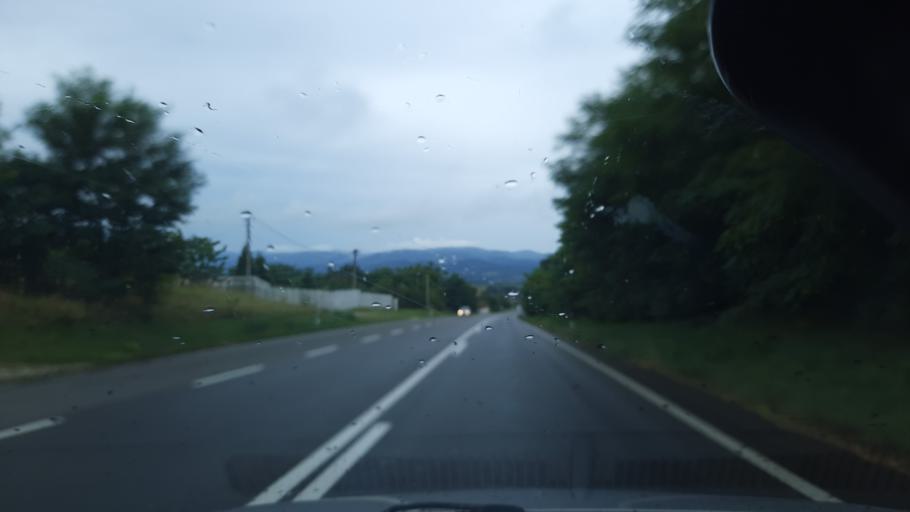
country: RS
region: Central Serbia
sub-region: Sumadijski Okrug
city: Knic
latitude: 43.9424
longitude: 20.7898
